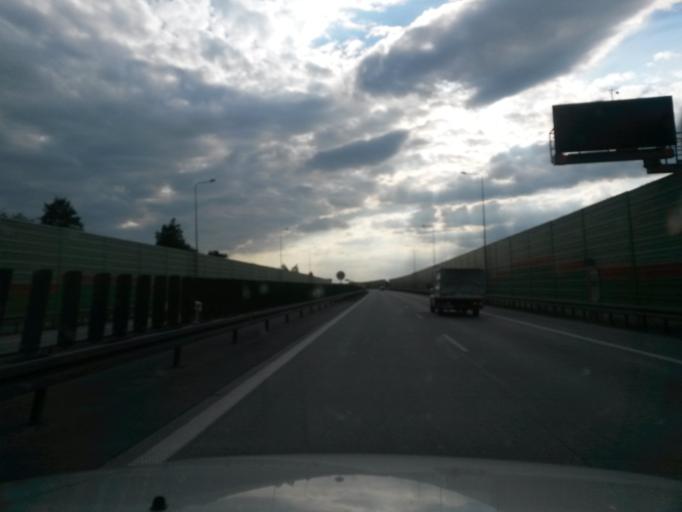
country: PL
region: Lodz Voivodeship
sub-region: Piotrkow Trybunalski
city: Piotrkow Trybunalski
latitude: 51.4422
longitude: 19.6643
